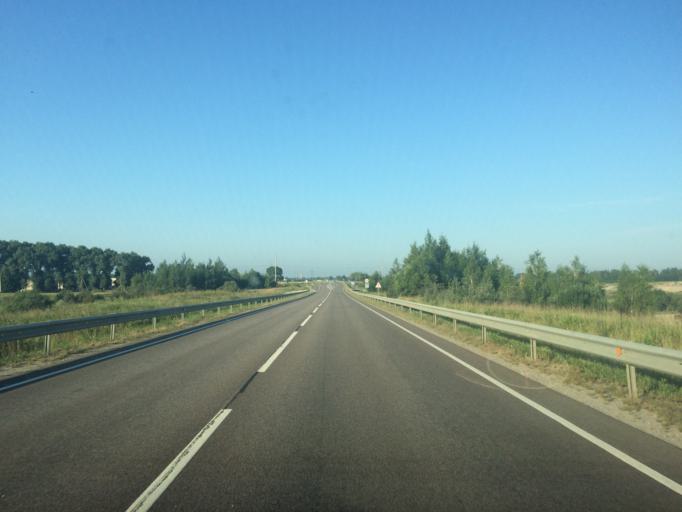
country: LT
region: Vilnius County
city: Ukmerge
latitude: 55.3269
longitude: 24.8818
